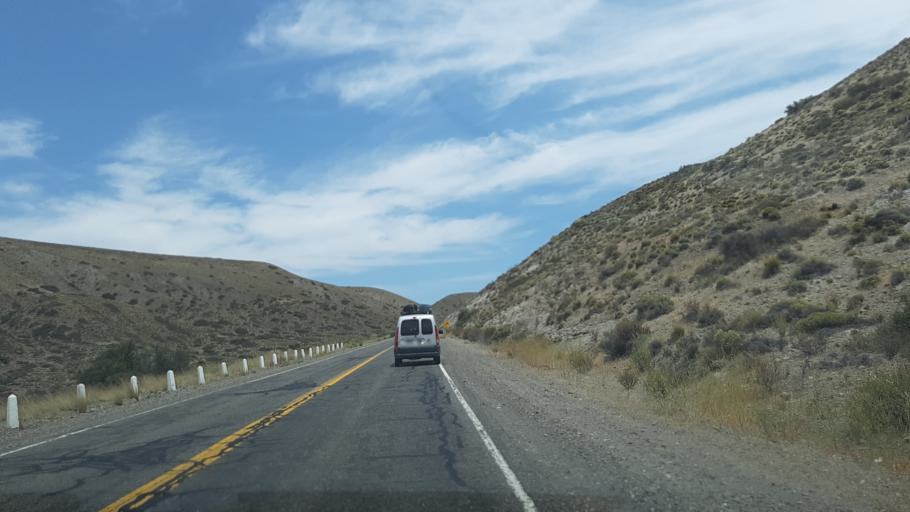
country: AR
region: Rio Negro
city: Pilcaniyeu
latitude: -40.4707
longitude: -70.6578
